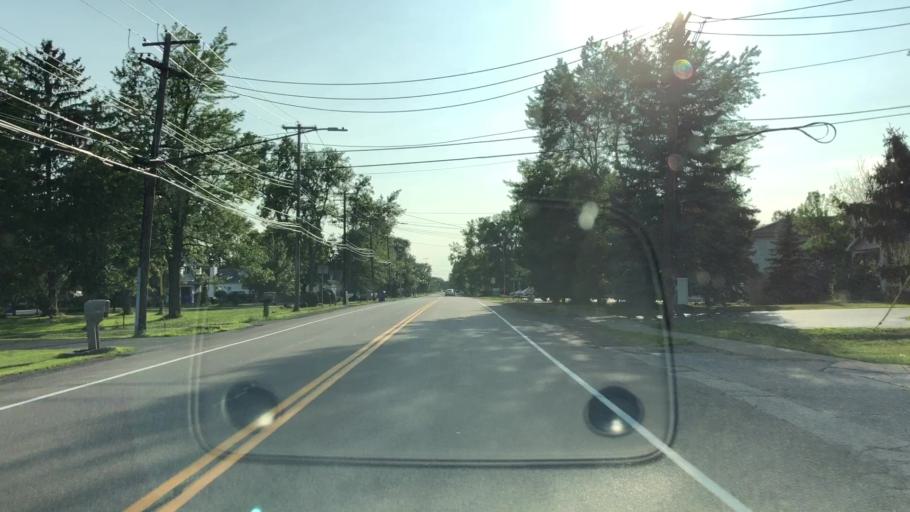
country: US
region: New York
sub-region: Erie County
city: Cheektowaga
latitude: 42.8570
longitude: -78.7328
